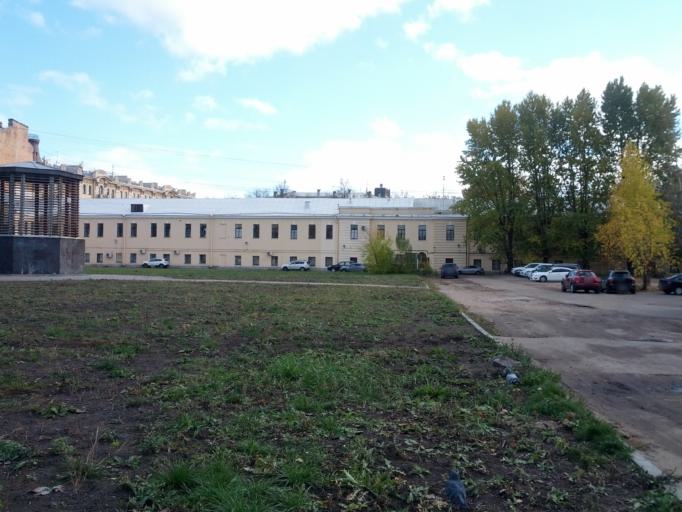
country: RU
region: St.-Petersburg
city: Saint Petersburg
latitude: 59.9237
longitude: 30.3327
